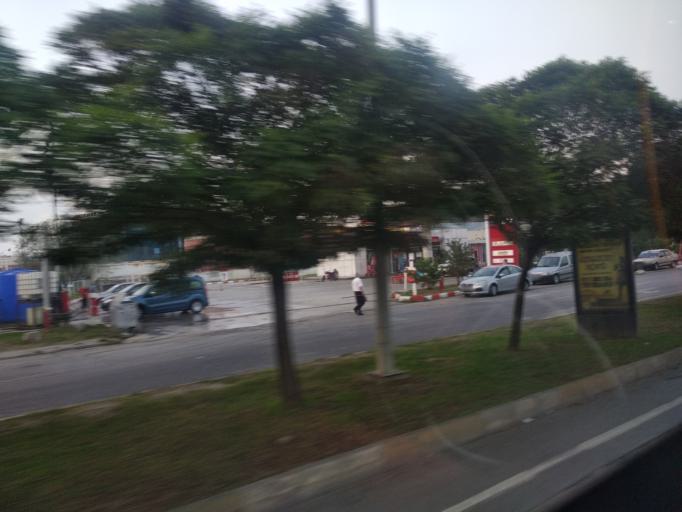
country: TR
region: Samsun
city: Samsun
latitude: 41.2859
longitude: 36.2888
